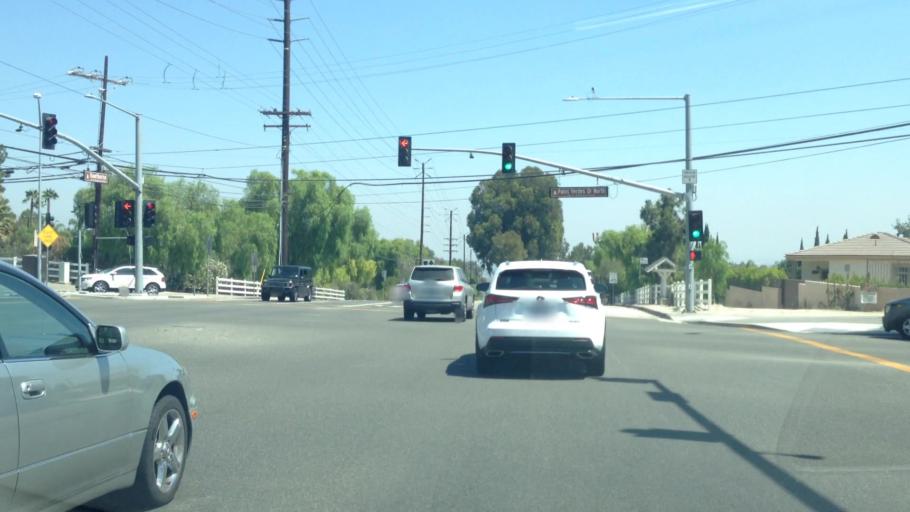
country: US
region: California
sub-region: Los Angeles County
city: Rolling Hills Estates
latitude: 33.7878
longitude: -118.3582
